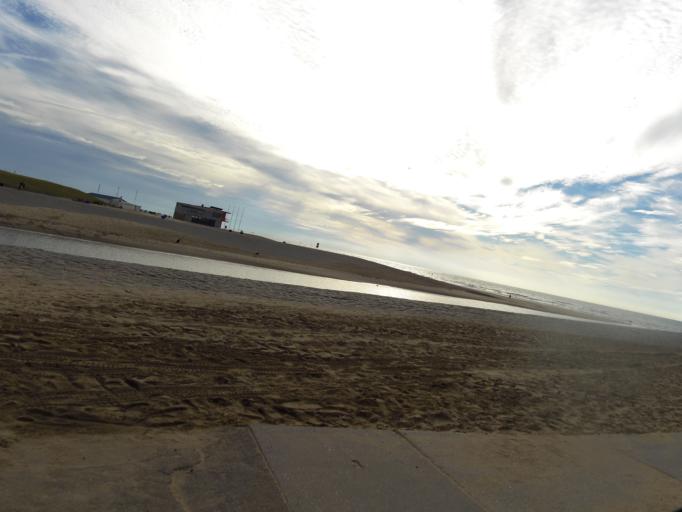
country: NL
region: South Holland
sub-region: Gemeente Katwijk
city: Katwijk aan Zee
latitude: 52.2118
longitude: 4.3999
